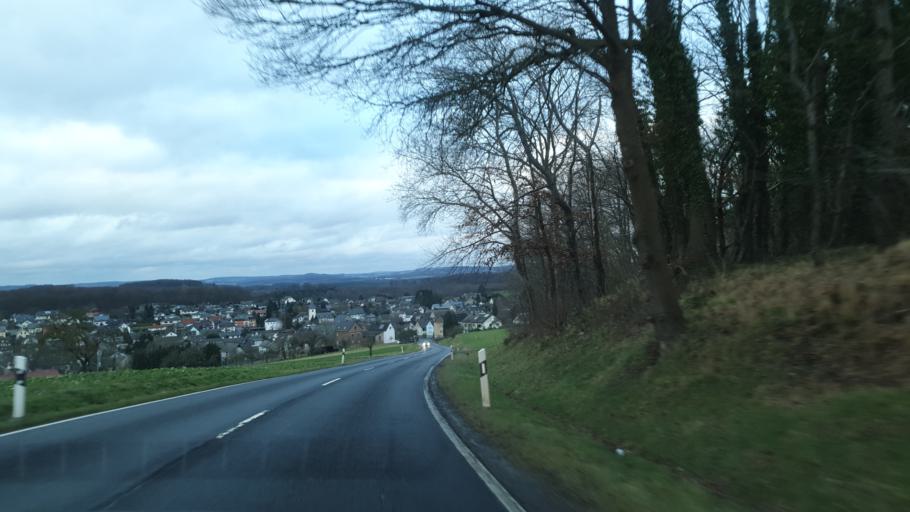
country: DE
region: Rheinland-Pfalz
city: Hirschberg
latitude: 50.3993
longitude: 7.9282
